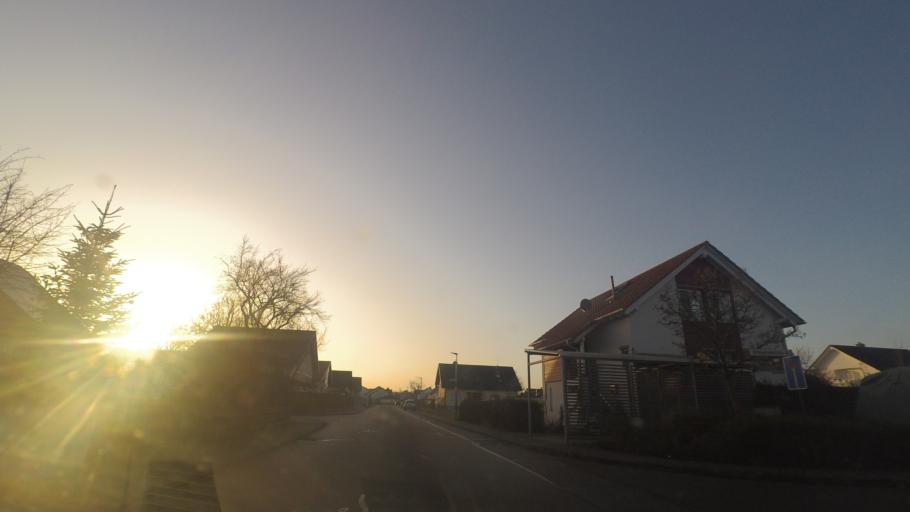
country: DE
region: Baden-Wuerttemberg
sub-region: Karlsruhe Region
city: Hambrucken
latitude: 49.1848
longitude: 8.5391
